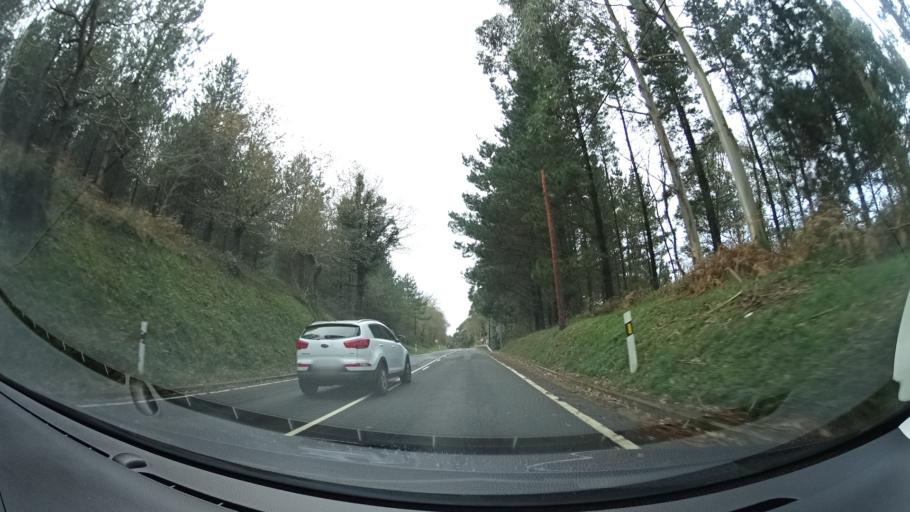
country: ES
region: Basque Country
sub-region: Bizkaia
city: Bermeo
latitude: 43.3973
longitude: -2.7614
